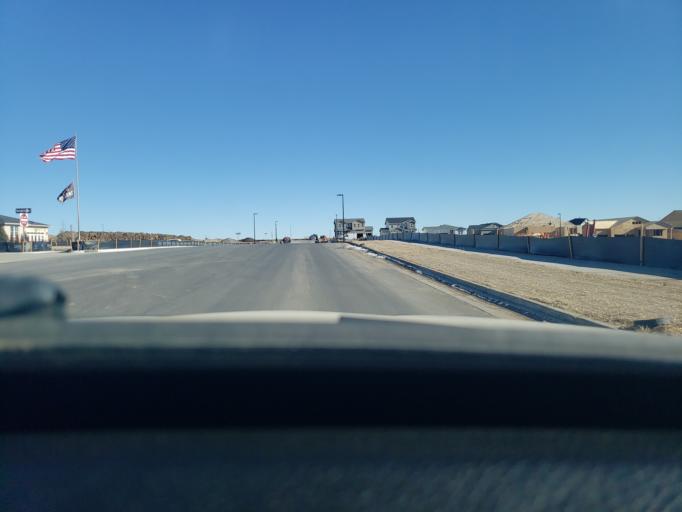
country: US
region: Colorado
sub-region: Adams County
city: Aurora
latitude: 39.7728
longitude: -104.7059
